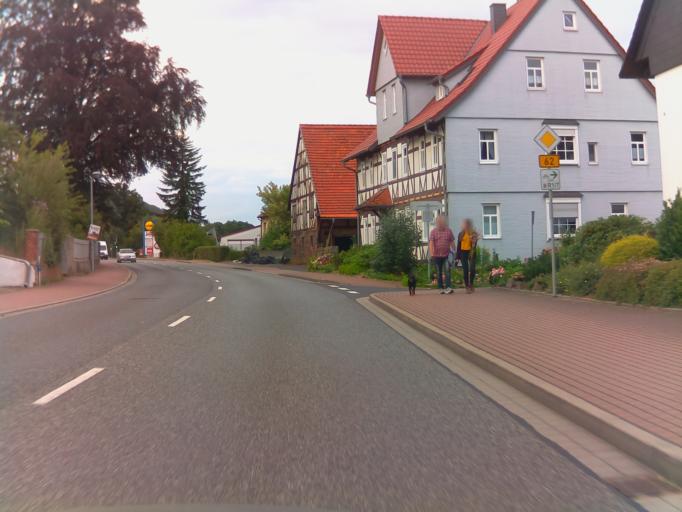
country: DE
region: Hesse
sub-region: Regierungsbezirk Kassel
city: Niederaula
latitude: 50.8022
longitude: 9.6109
